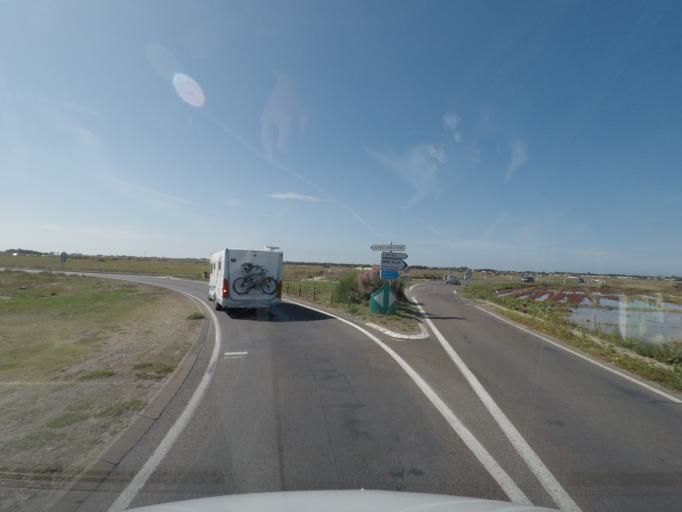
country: FR
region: Pays de la Loire
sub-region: Departement de la Vendee
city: La Gueriniere
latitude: 46.9909
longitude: -2.2509
